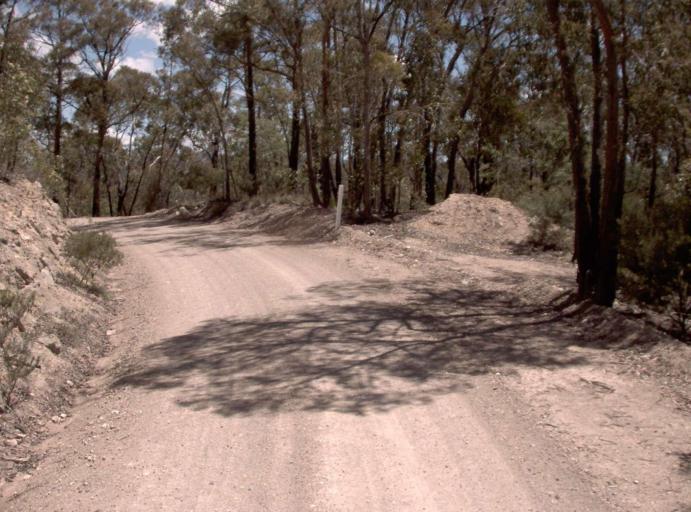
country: AU
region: New South Wales
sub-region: Snowy River
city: Jindabyne
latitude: -37.0856
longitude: 148.3274
